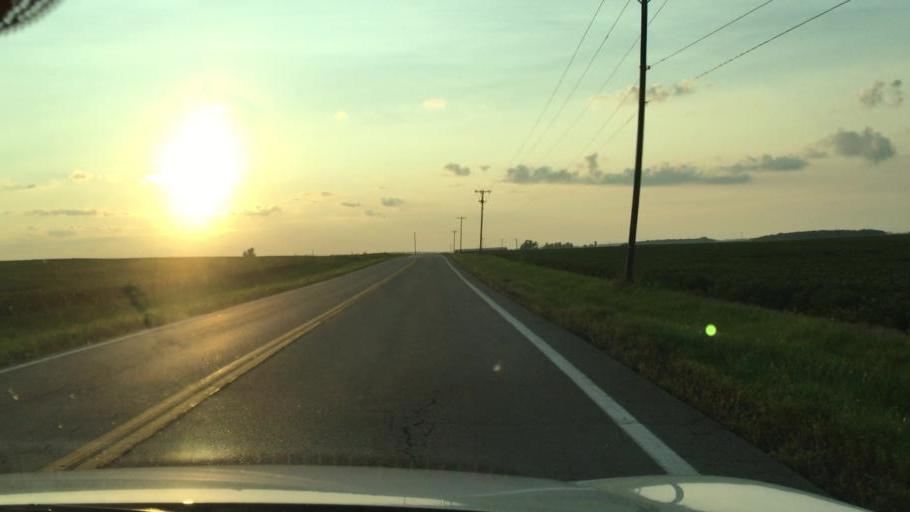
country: US
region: Ohio
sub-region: Madison County
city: Choctaw Lake
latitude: 39.9897
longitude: -83.4136
